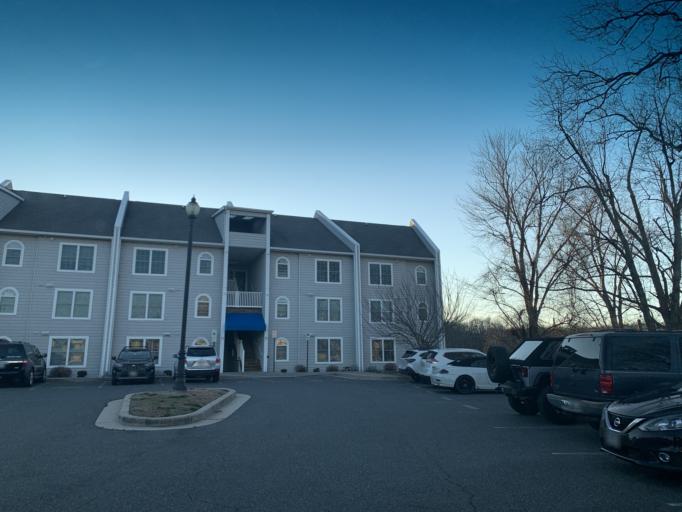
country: US
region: Maryland
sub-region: Cecil County
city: Perryville
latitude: 39.5606
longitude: -76.0808
